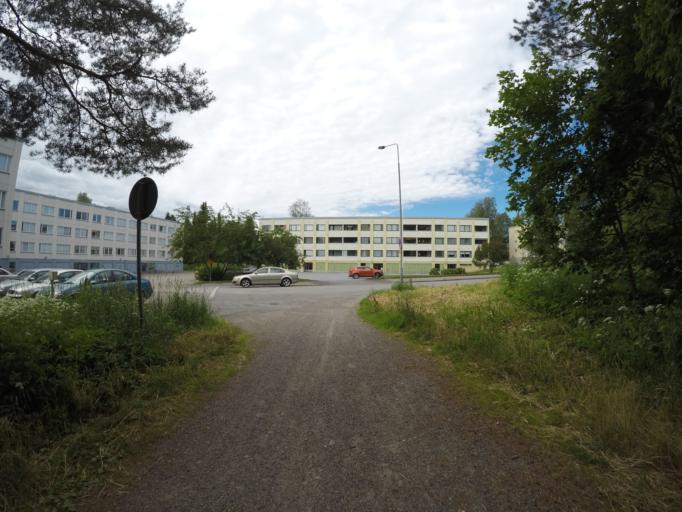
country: FI
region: Haeme
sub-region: Haemeenlinna
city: Haemeenlinna
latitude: 61.0049
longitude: 24.4438
